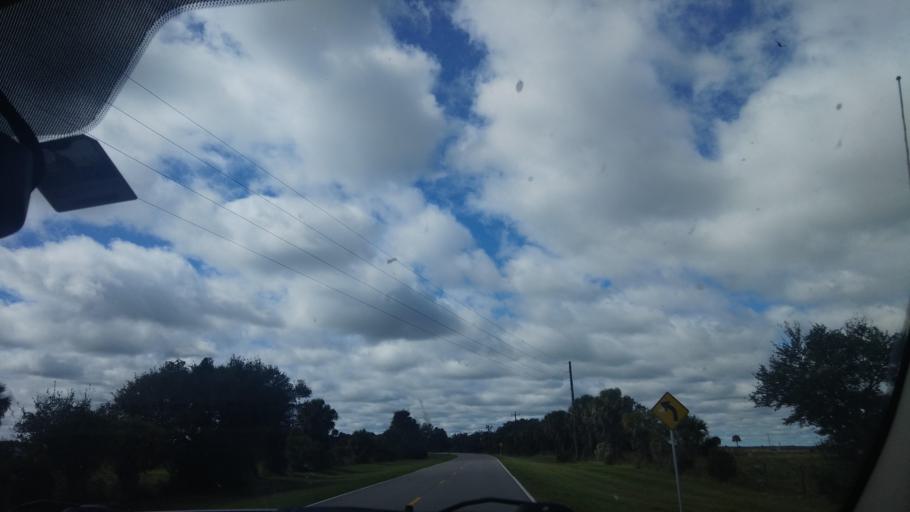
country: US
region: Florida
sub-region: Okeechobee County
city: Okeechobee
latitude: 27.3948
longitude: -80.9101
